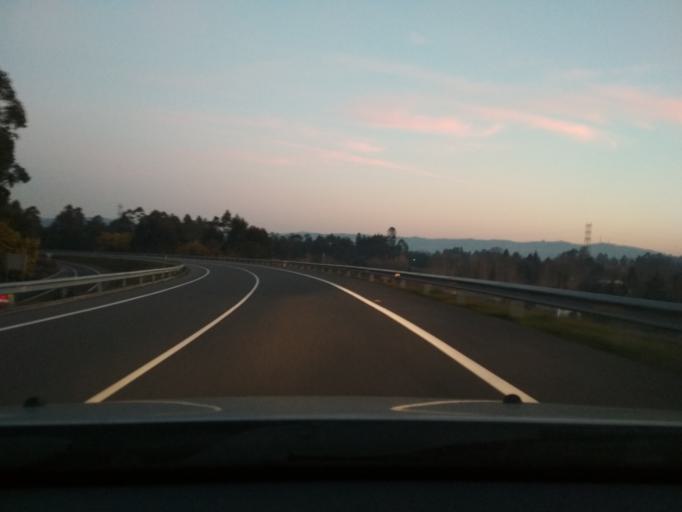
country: ES
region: Galicia
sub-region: Provincia da Coruna
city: Santiago de Compostela
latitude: 42.8461
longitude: -8.5938
